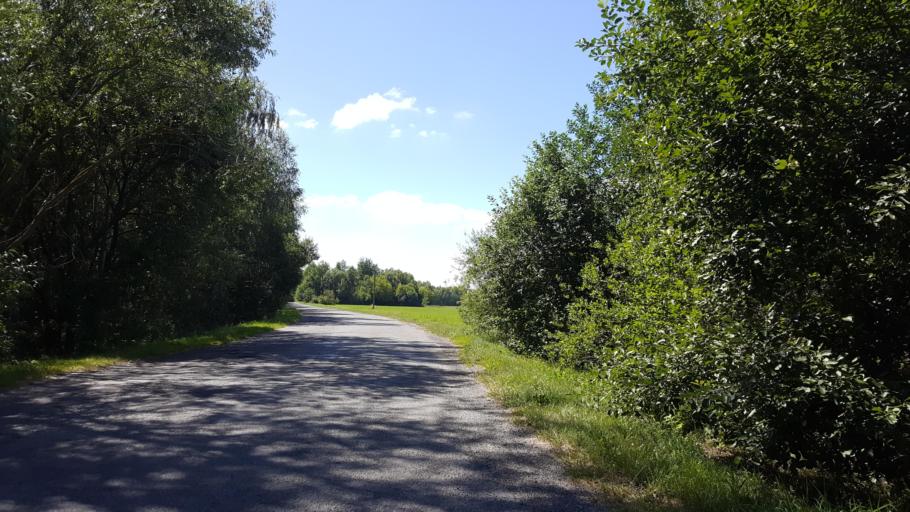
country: BY
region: Brest
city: Horad Kobryn
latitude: 52.3000
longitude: 24.3625
